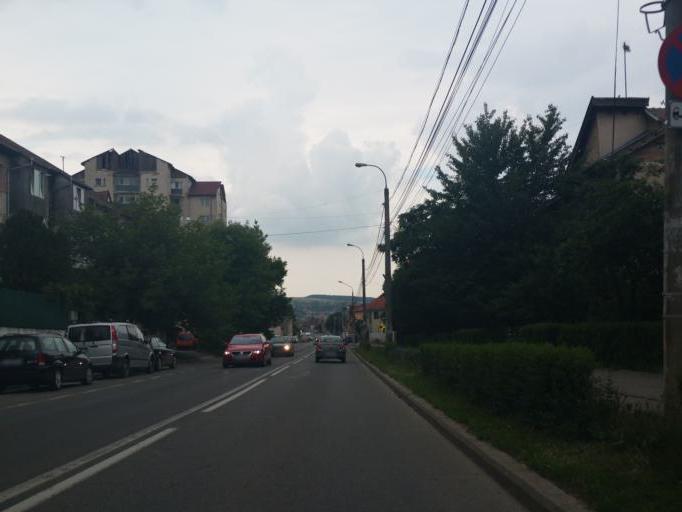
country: RO
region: Salaj
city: Zalau
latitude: 47.1711
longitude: 23.0664
